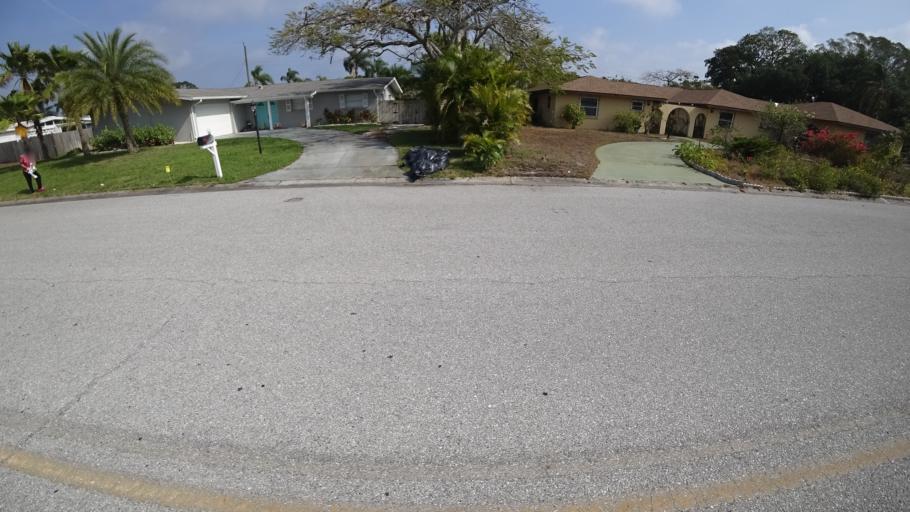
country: US
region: Florida
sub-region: Manatee County
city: West Bradenton
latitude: 27.4927
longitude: -82.6194
